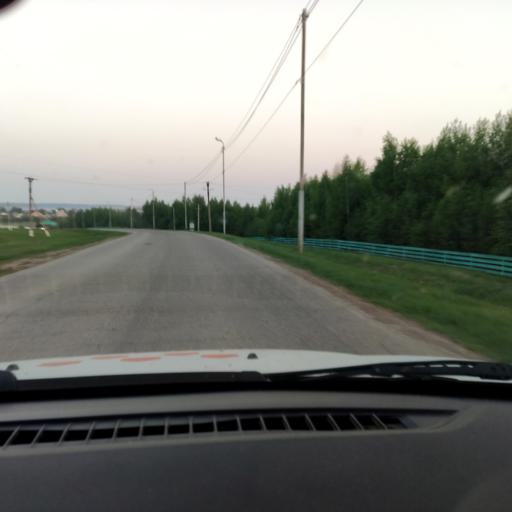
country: RU
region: Bashkortostan
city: Karmaskaly
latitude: 54.3755
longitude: 56.1511
